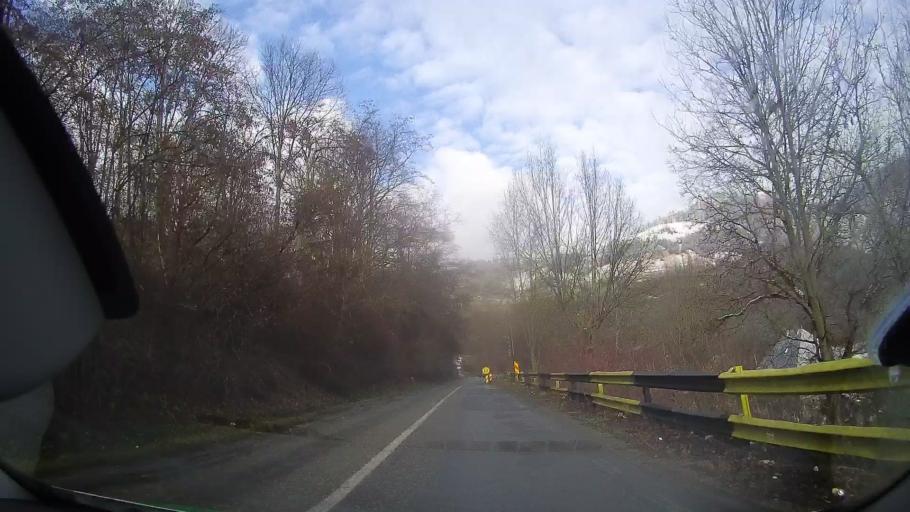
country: RO
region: Alba
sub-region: Comuna Lupsa
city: Lupsa
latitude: 46.3810
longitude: 23.2308
